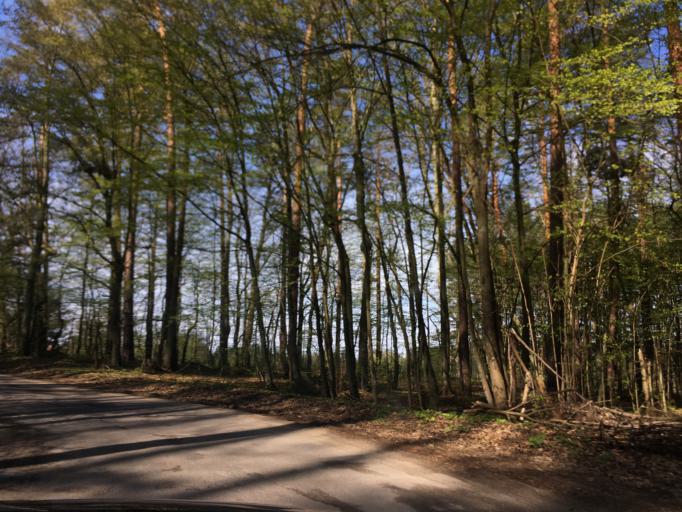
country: PL
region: Warmian-Masurian Voivodeship
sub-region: Powiat piski
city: Ruciane-Nida
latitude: 53.6873
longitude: 21.5890
